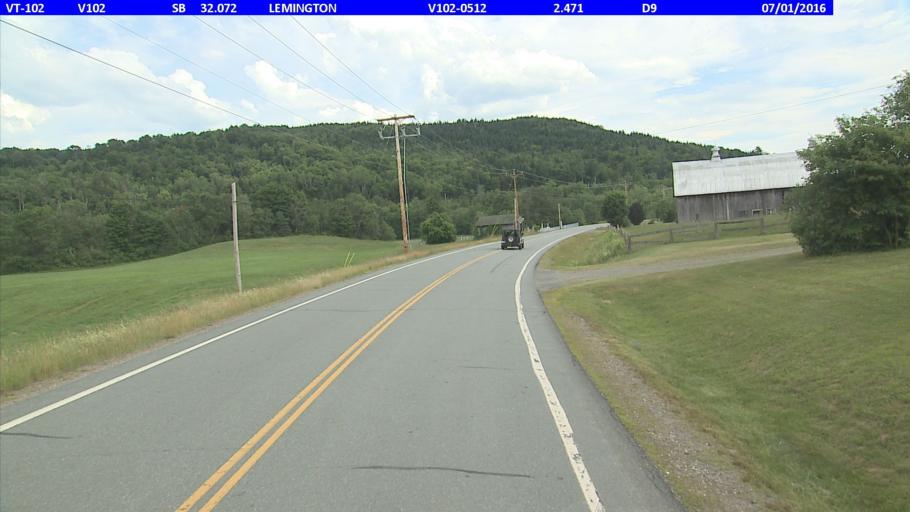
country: US
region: New Hampshire
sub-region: Coos County
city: Colebrook
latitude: 44.8578
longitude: -71.5509
